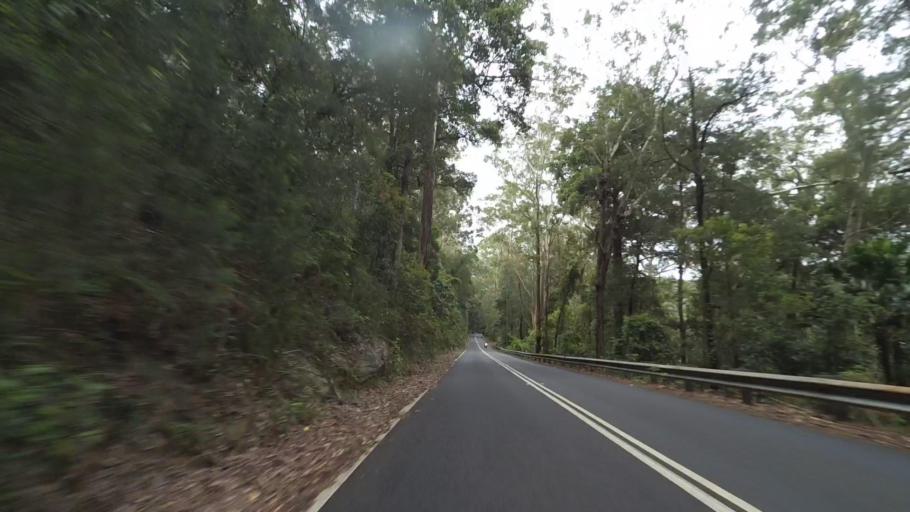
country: AU
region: New South Wales
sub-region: Wollongong
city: Helensburgh
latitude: -34.1528
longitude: 151.0328
